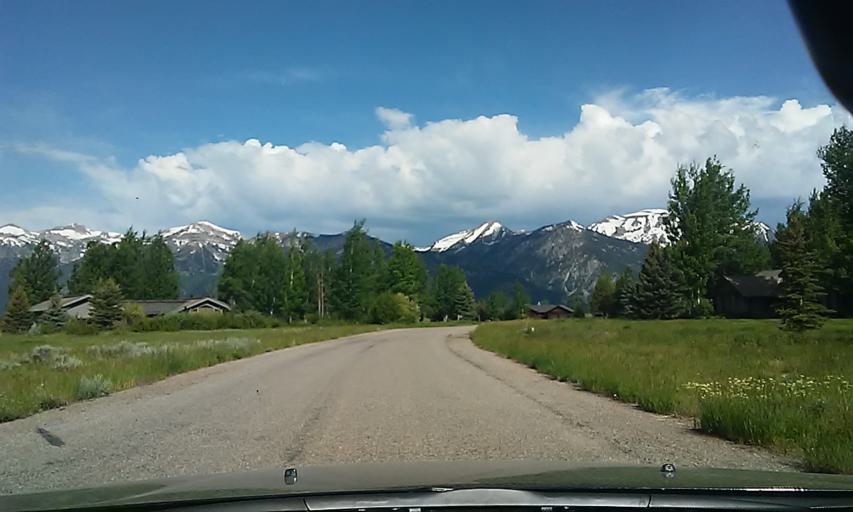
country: US
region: Wyoming
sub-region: Teton County
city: Jackson
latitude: 43.5777
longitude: -110.7554
